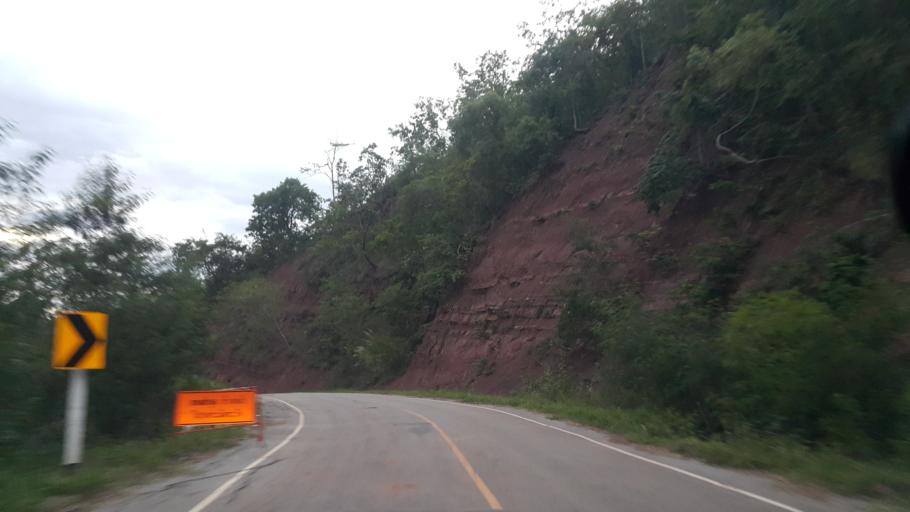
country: TH
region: Loei
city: Phu Ruea
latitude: 17.5140
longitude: 101.2320
